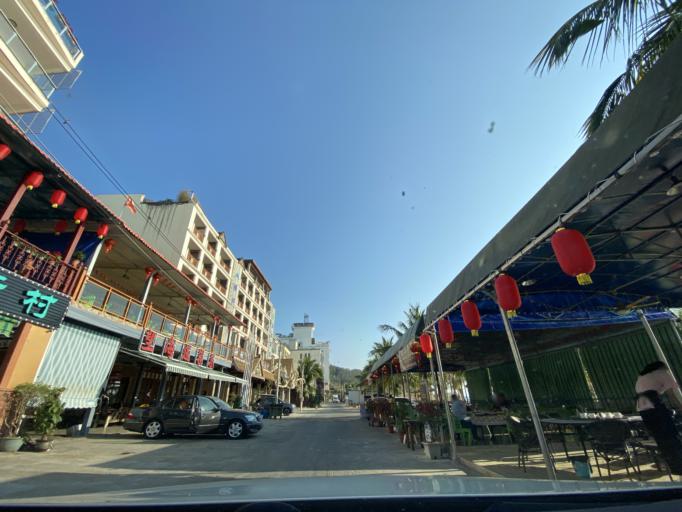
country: CN
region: Hainan
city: Yingzhou
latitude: 18.3887
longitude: 109.8177
